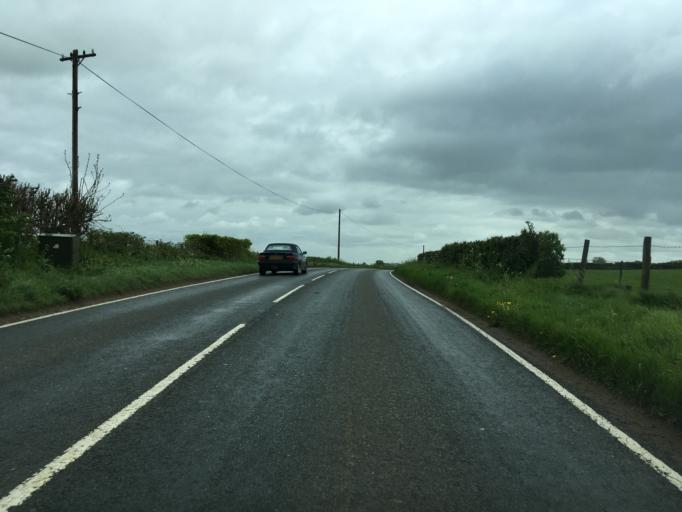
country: GB
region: England
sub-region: Bath and North East Somerset
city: Stanton Drew
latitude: 51.3474
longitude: -2.5737
